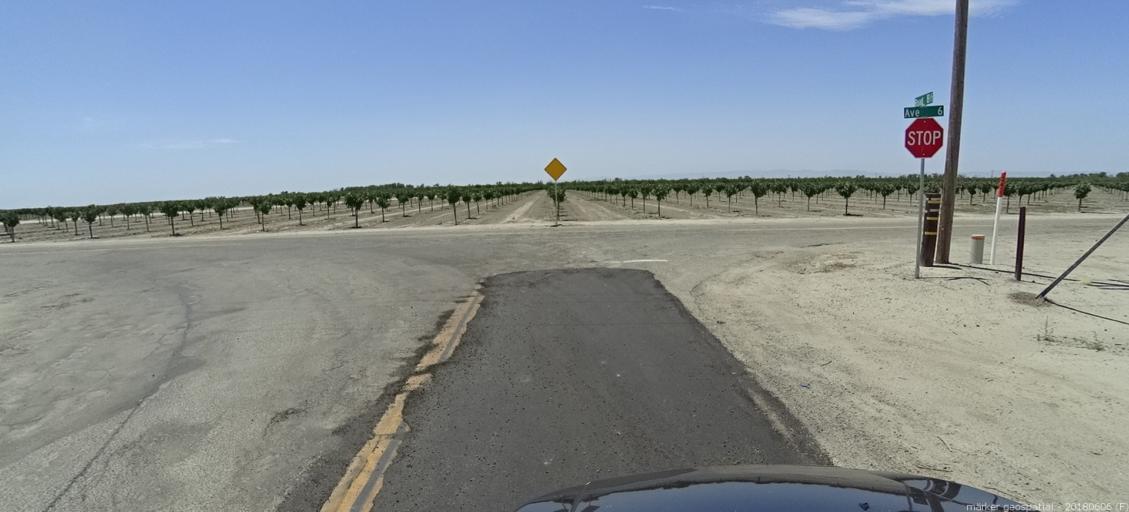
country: US
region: California
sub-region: Fresno County
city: Firebaugh
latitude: 36.8369
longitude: -120.3913
